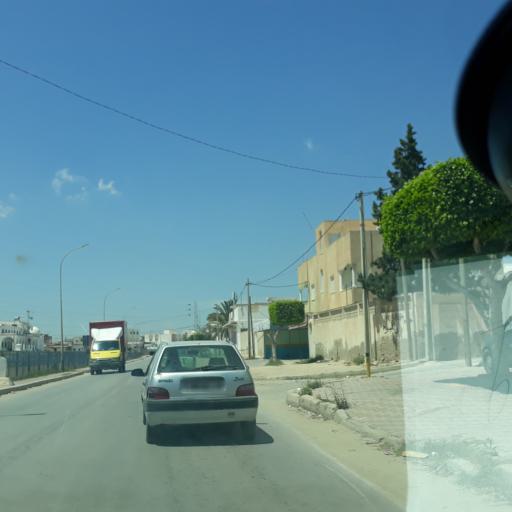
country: TN
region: Safaqis
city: Al Qarmadah
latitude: 34.8075
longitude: 10.7529
